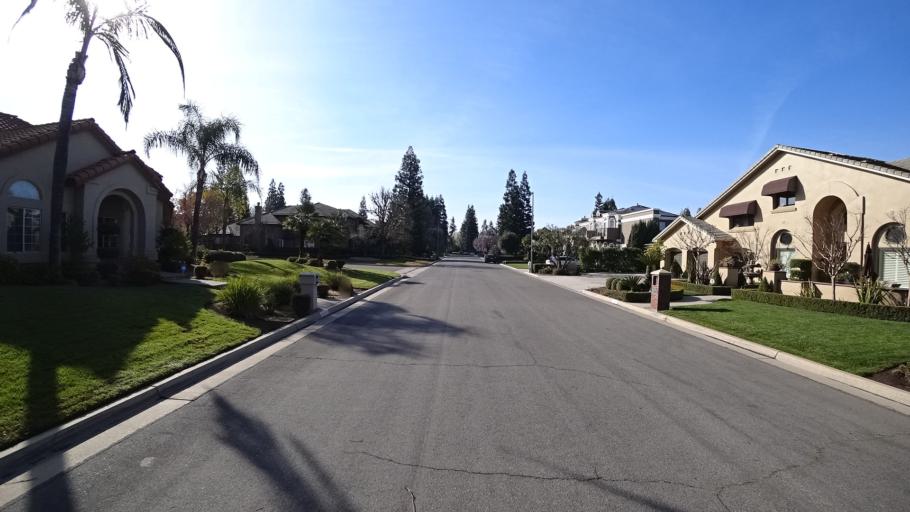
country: US
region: California
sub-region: Fresno County
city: Clovis
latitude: 36.8833
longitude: -119.7640
